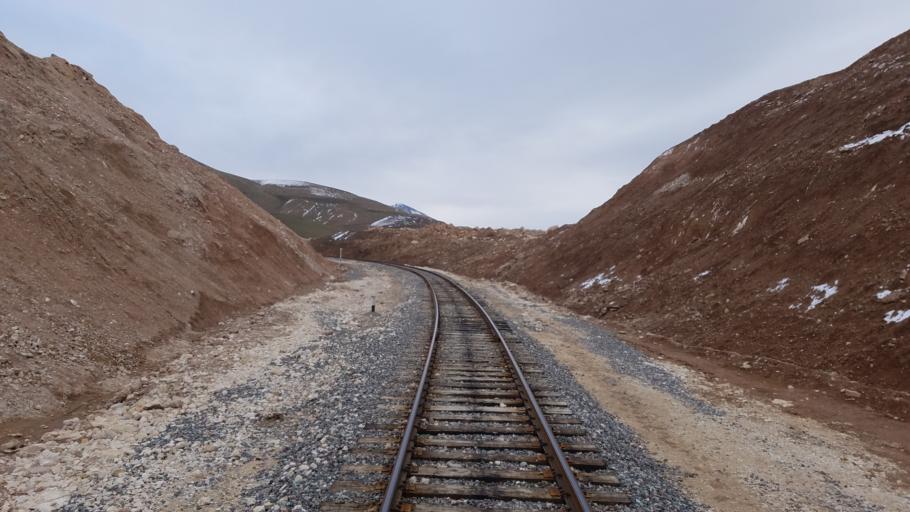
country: TJ
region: Khatlon
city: Yovon
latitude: 38.3879
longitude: 68.9381
